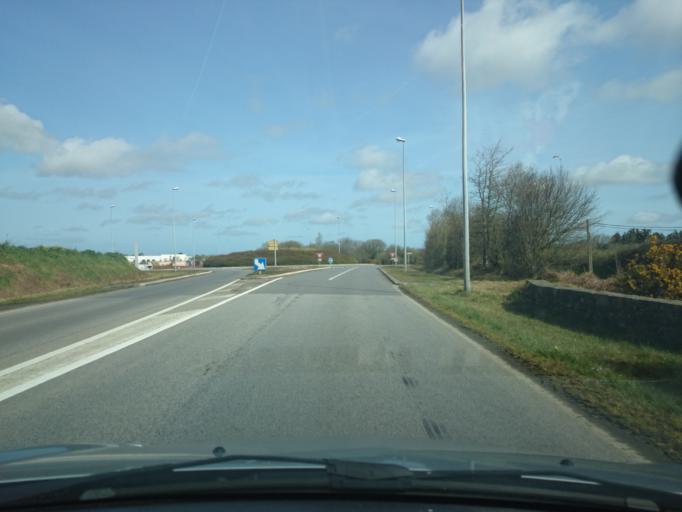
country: FR
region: Brittany
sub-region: Departement du Finistere
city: Gouesnou
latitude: 48.4551
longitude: -4.4479
